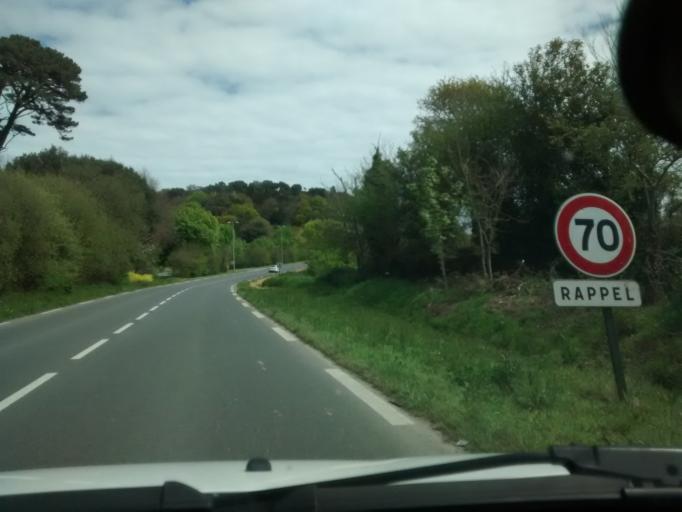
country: FR
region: Brittany
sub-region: Departement des Cotes-d'Armor
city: Ploubazlanec
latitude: 48.7923
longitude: -3.0426
